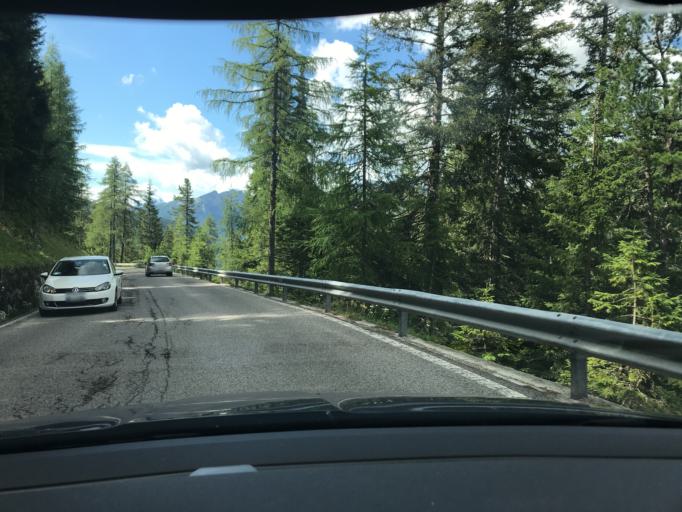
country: IT
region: Veneto
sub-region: Provincia di Belluno
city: Livinallongo del Col di Lana
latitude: 46.4995
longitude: 11.9923
